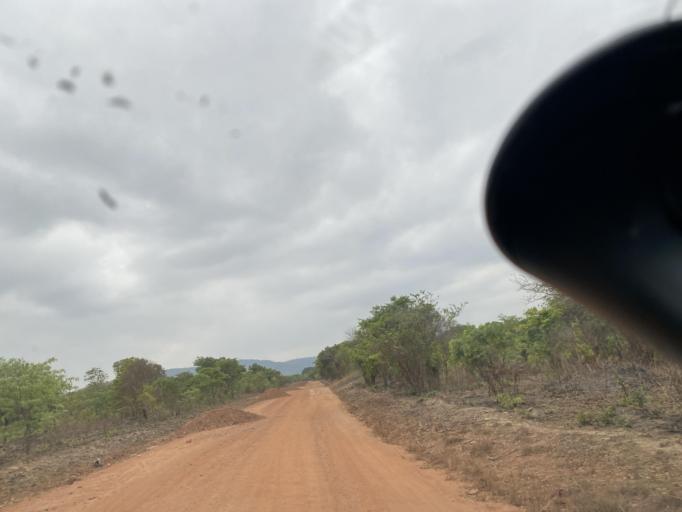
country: ZM
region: Lusaka
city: Chongwe
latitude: -15.2094
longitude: 28.7580
